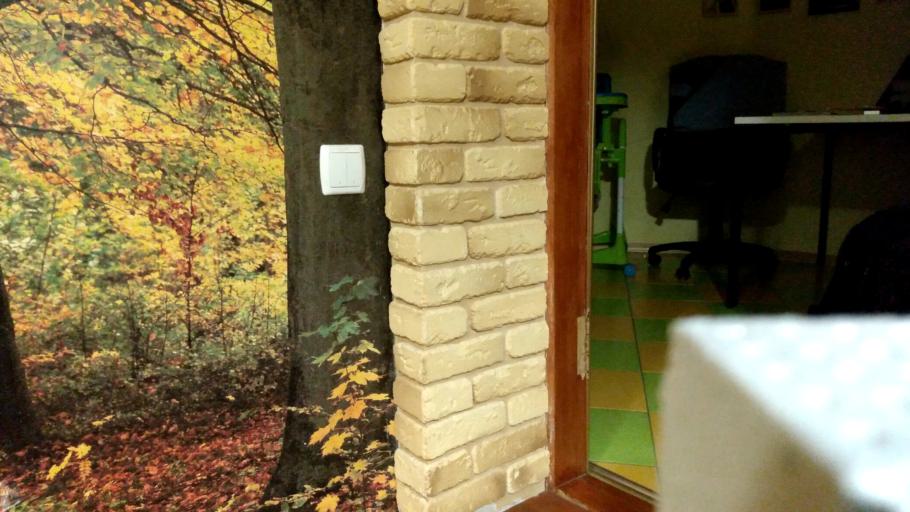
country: RU
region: Arkhangelskaya
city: Kargopol'
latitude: 61.5163
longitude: 37.7743
